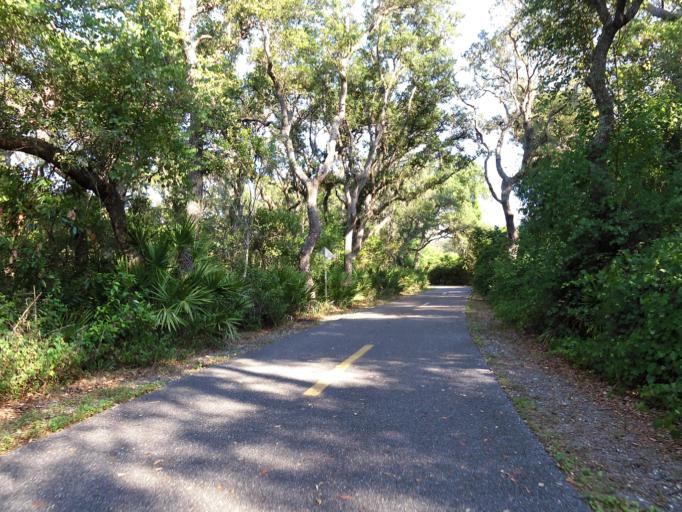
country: US
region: Florida
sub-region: Nassau County
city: Fernandina Beach
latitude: 30.4992
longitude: -81.4488
